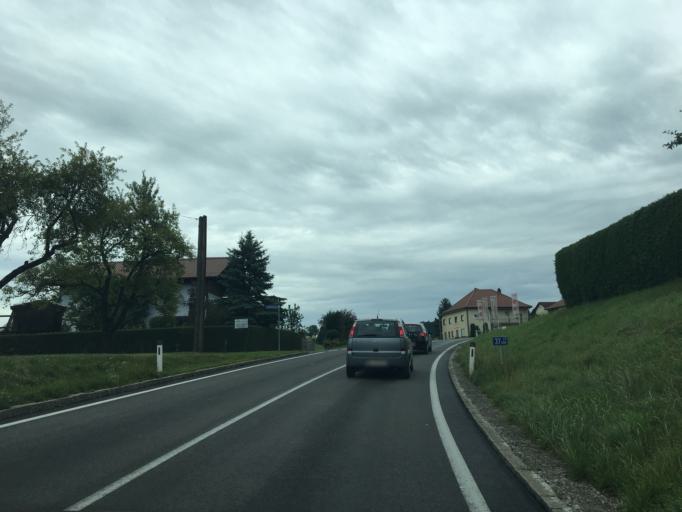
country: AT
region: Salzburg
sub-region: Politischer Bezirk Salzburg-Umgebung
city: Dorfbeuern
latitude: 48.0709
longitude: 12.9886
